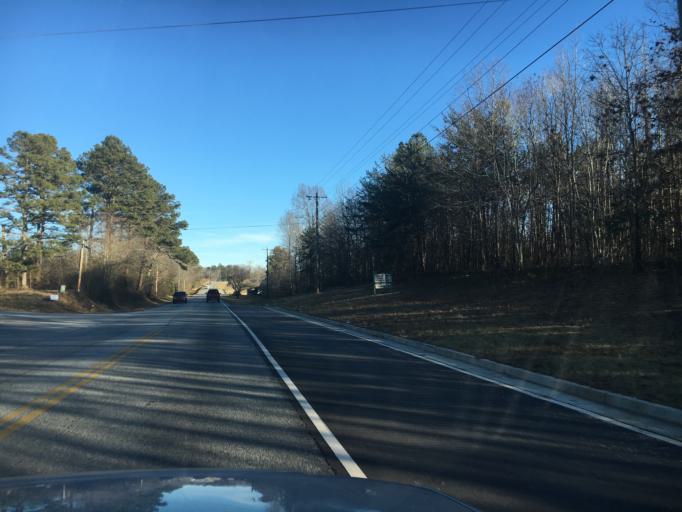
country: US
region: Georgia
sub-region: Habersham County
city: Demorest
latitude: 34.5496
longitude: -83.5617
